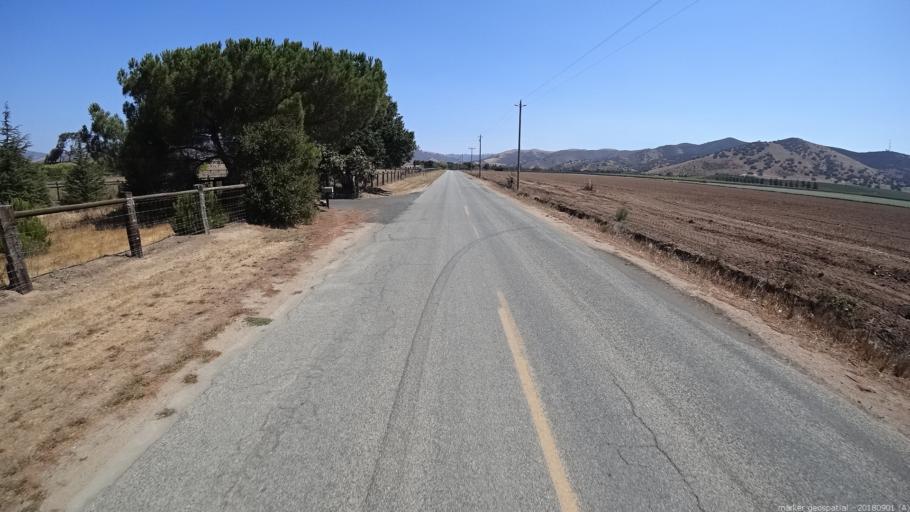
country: US
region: California
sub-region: Monterey County
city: Chualar
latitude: 36.5886
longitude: -121.4617
